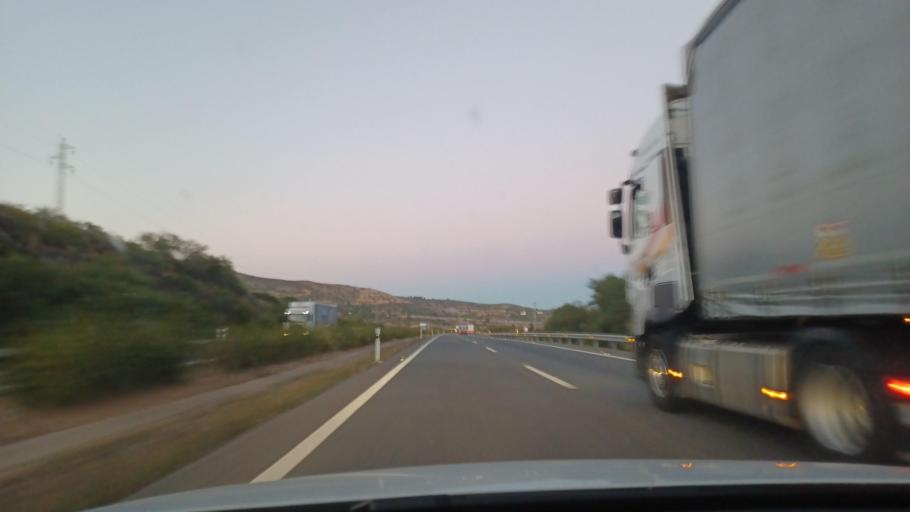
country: ES
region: Valencia
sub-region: Provincia de Castello
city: Torreblanca
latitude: 40.2175
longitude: 0.1853
